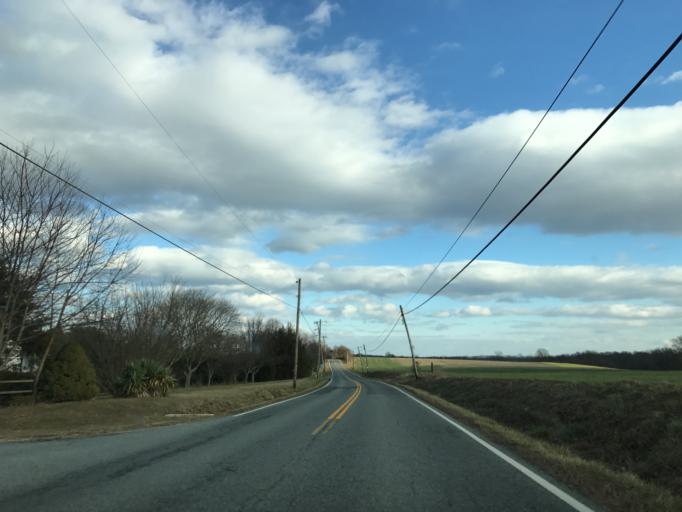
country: US
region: Maryland
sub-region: Cecil County
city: Rising Sun
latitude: 39.6348
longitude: -76.0579
